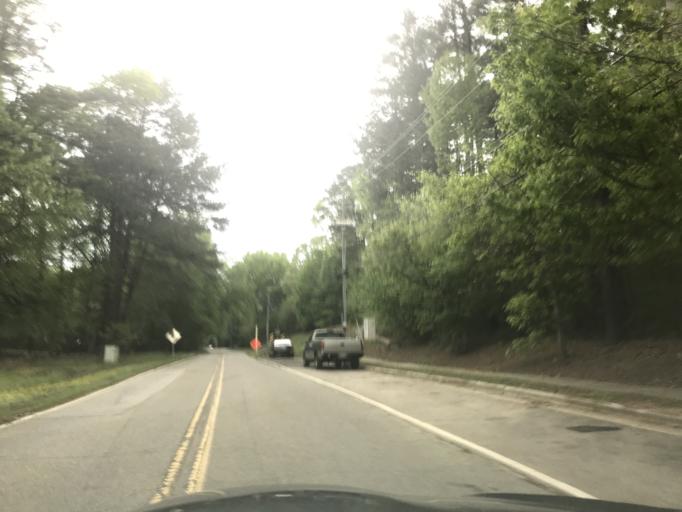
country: US
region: North Carolina
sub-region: Wake County
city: West Raleigh
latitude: 35.7636
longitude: -78.7039
